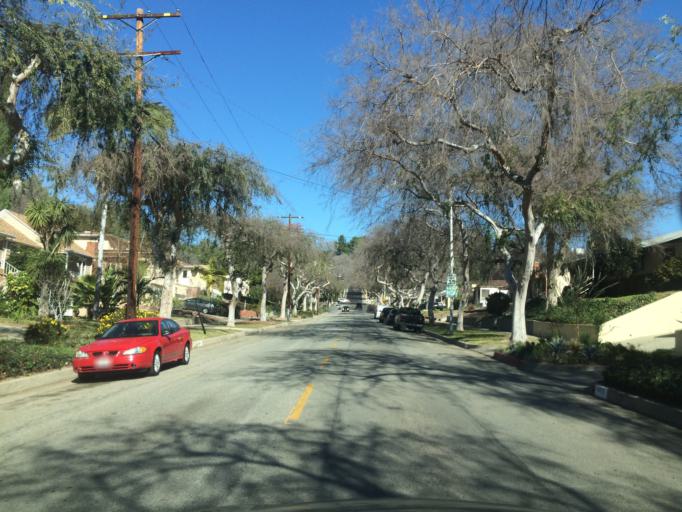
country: US
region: California
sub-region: Los Angeles County
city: South Pasadena
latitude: 34.1017
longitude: -118.1781
